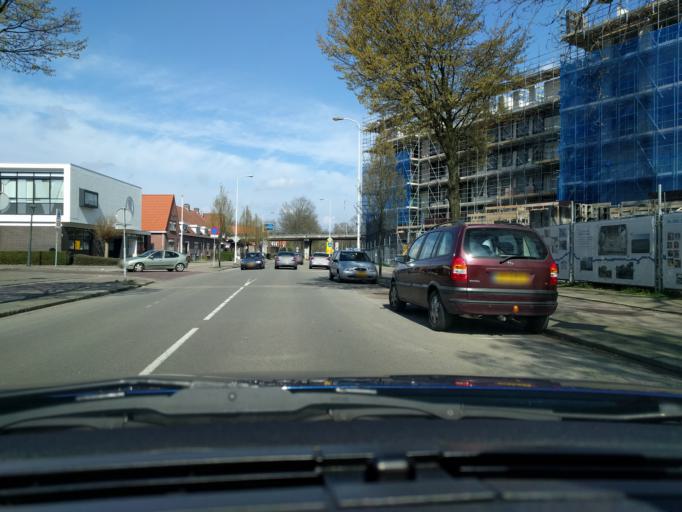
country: NL
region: North Brabant
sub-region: Gemeente Eindhoven
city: Eindhoven
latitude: 51.4471
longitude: 5.4527
